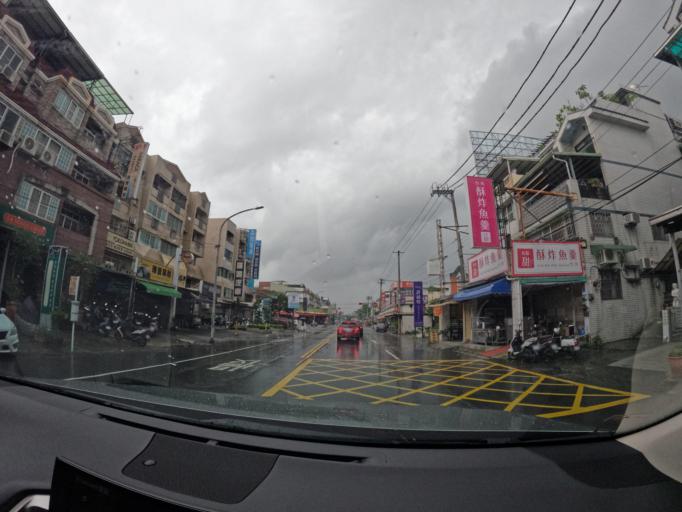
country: TW
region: Taiwan
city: Fengshan
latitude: 22.6551
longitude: 120.3366
